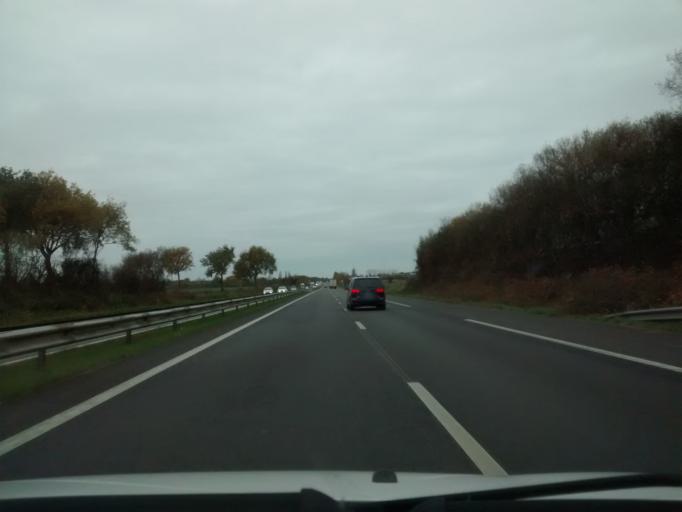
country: FR
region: Brittany
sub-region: Departement d'Ille-et-Vilaine
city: Chateaubourg
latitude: 48.0951
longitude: -1.4013
